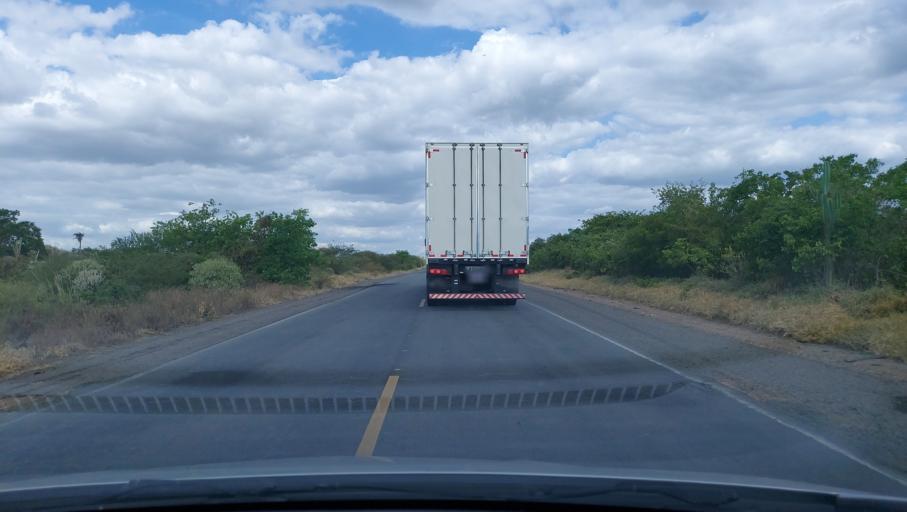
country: BR
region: Bahia
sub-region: Ipira
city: Ipira
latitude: -12.4893
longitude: -39.7974
